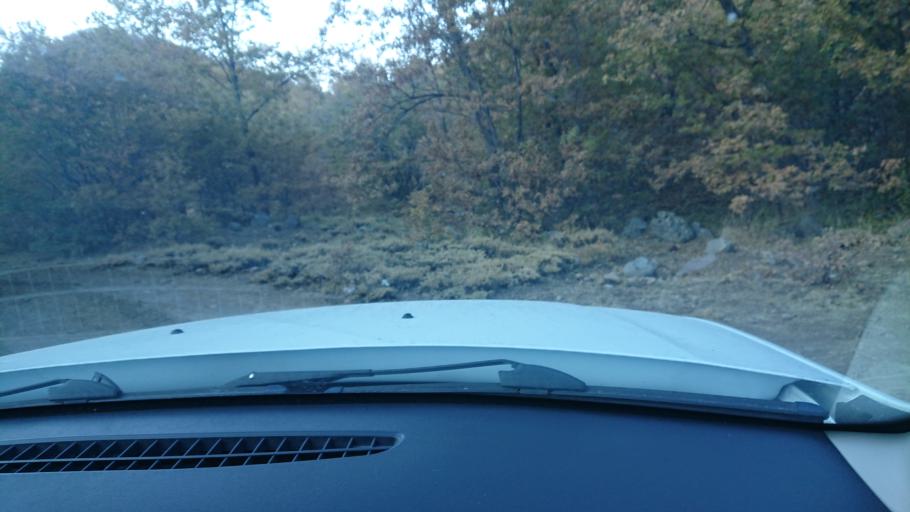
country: TR
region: Aksaray
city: Taspinar
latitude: 38.1645
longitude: 34.2101
